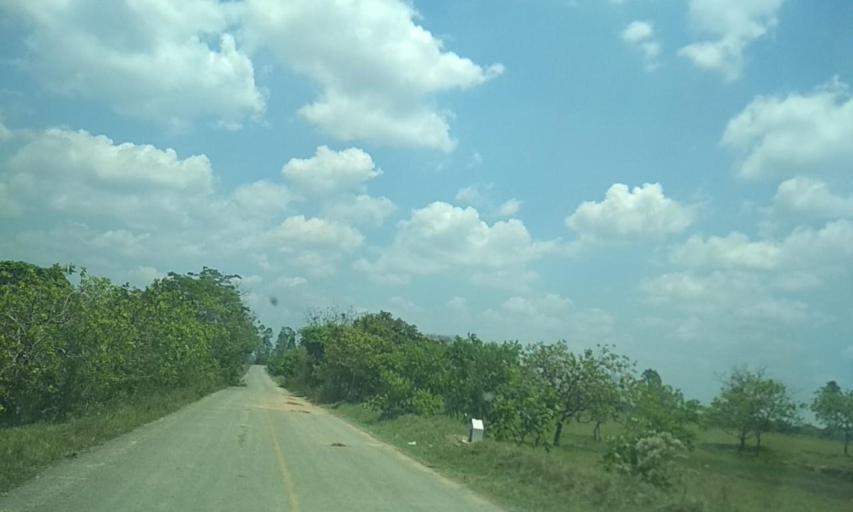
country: MX
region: Tabasco
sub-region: Huimanguillo
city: Francisco Rueda
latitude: 17.8072
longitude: -93.8657
